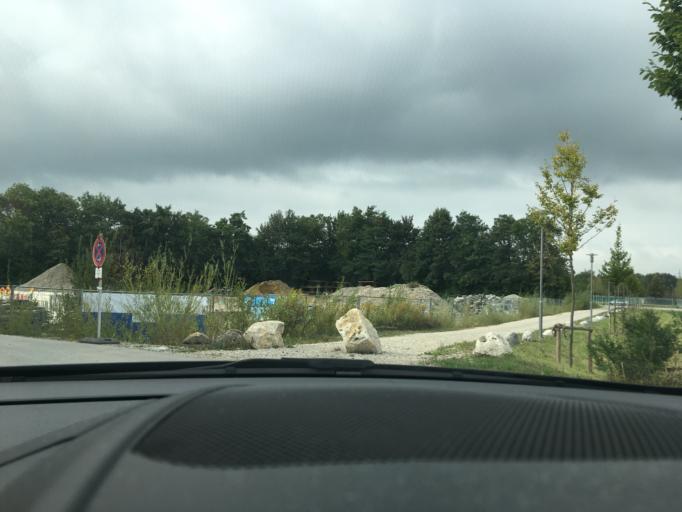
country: DE
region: Bavaria
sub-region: Upper Bavaria
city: Ismaning
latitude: 48.2394
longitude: 11.6840
